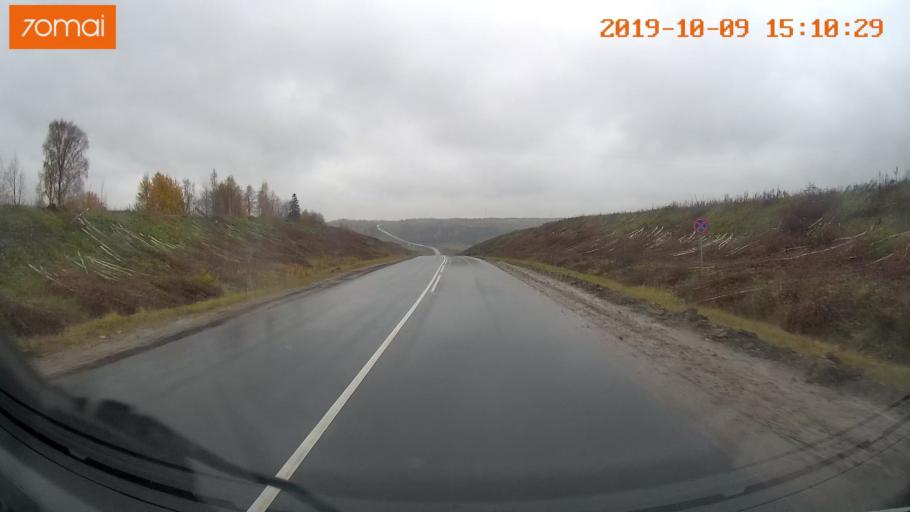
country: RU
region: Kostroma
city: Susanino
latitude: 58.1775
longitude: 41.6407
